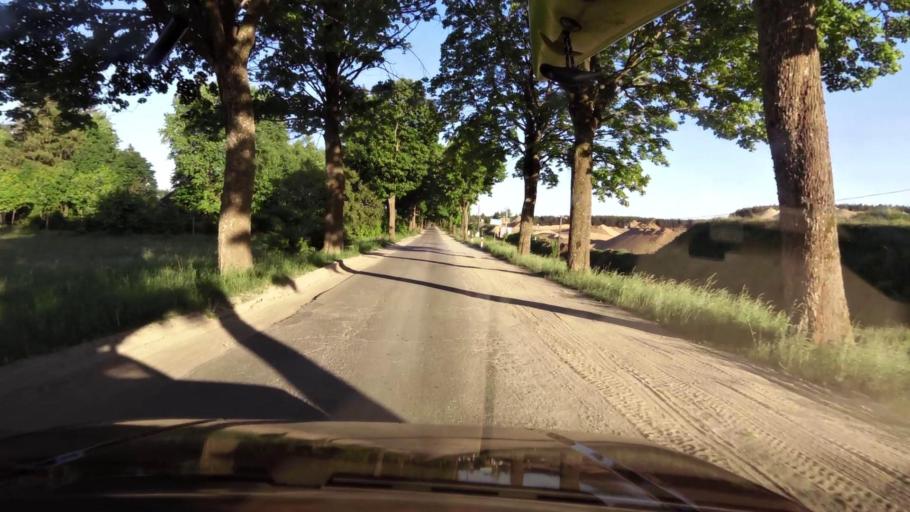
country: PL
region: West Pomeranian Voivodeship
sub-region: Powiat szczecinecki
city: Bialy Bor
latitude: 53.9382
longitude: 16.7909
